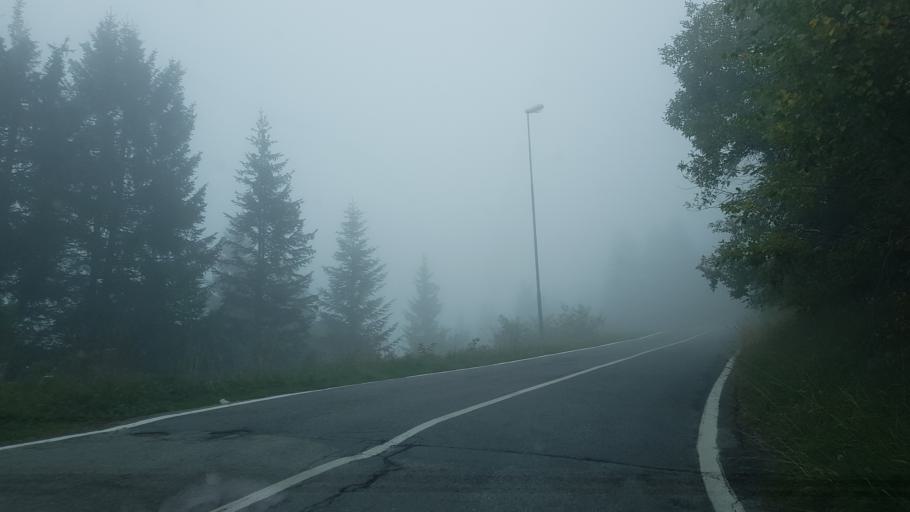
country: IT
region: Piedmont
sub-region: Provincia di Cuneo
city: Frabosa Soprana
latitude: 44.2570
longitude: 7.7906
